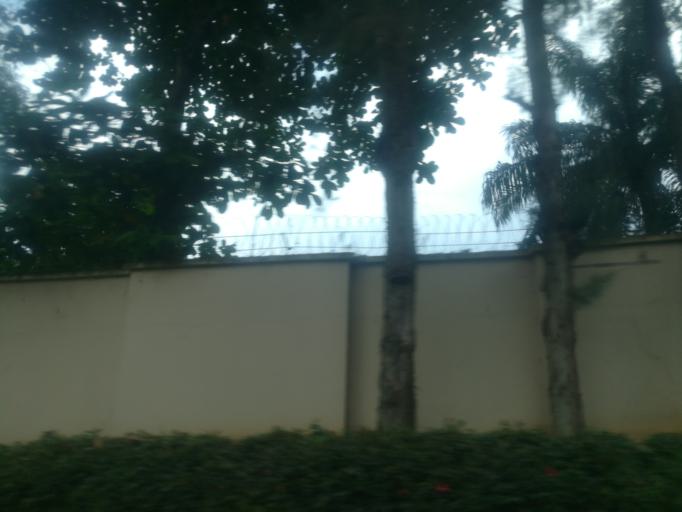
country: NG
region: Oyo
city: Ibadan
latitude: 7.4210
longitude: 3.9056
